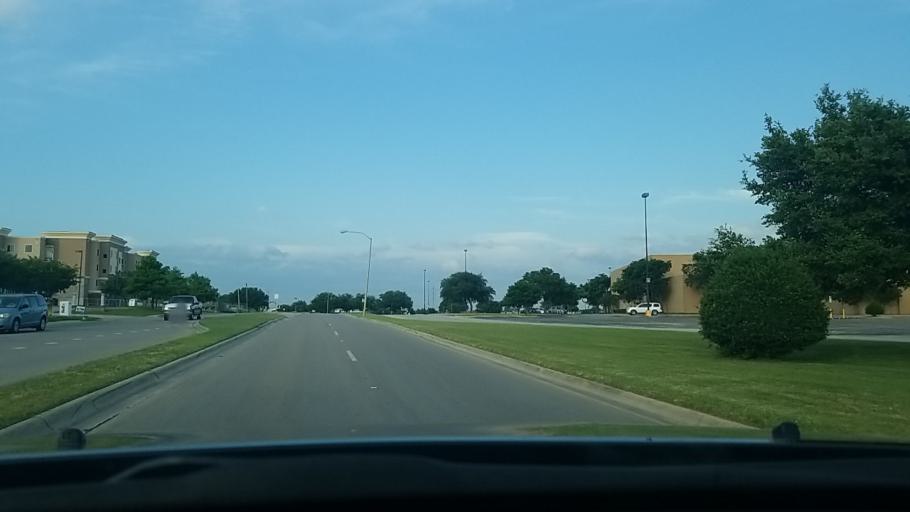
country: US
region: Texas
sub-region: Denton County
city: Denton
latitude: 33.1920
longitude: -97.1100
